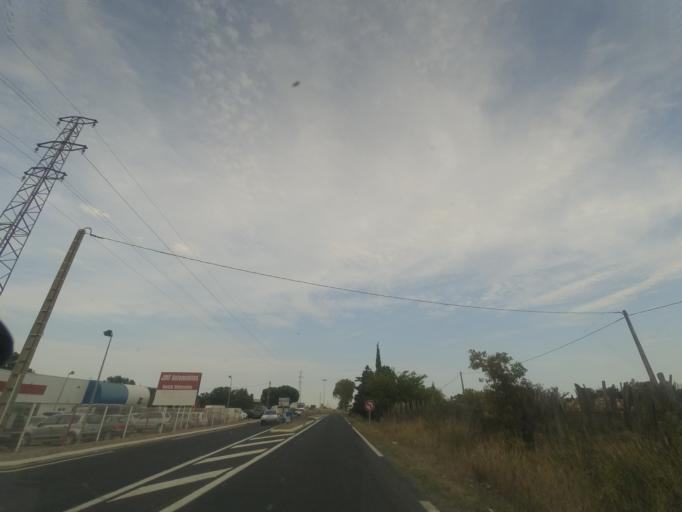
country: FR
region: Languedoc-Roussillon
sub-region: Departement des Pyrenees-Orientales
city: Baho
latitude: 42.6896
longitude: 2.8321
